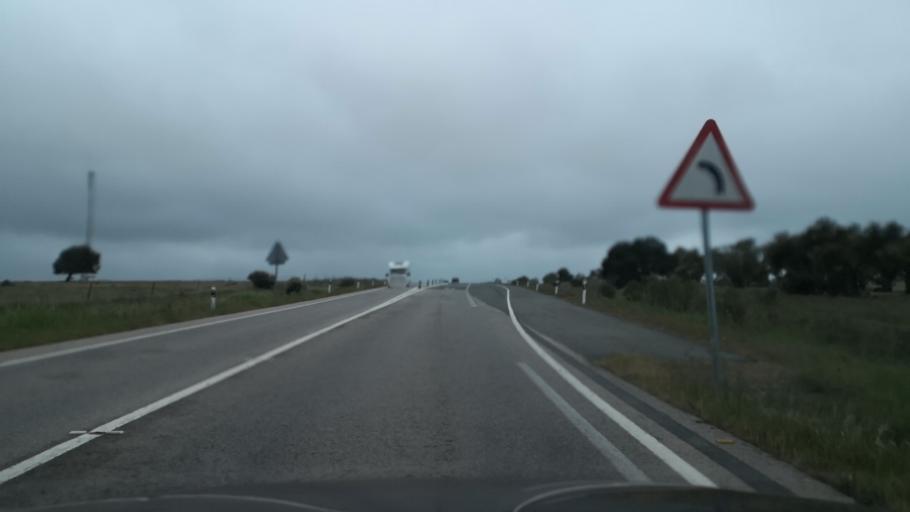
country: ES
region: Extremadura
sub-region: Provincia de Caceres
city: Malpartida de Caceres
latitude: 39.3651
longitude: -6.4602
